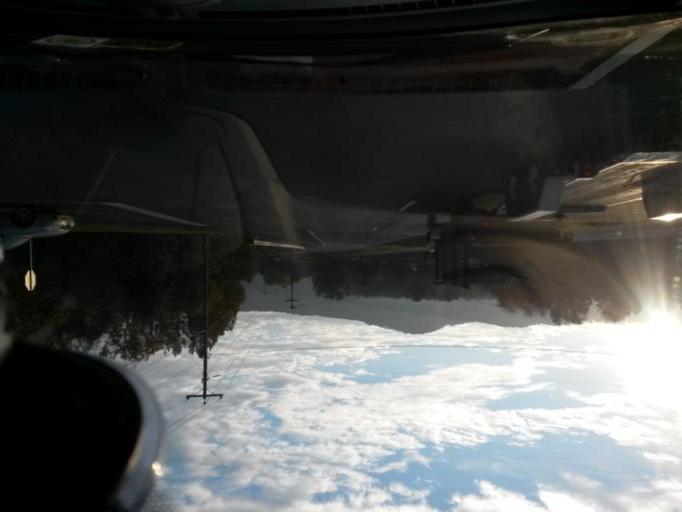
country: US
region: Virginia
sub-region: Botetourt County
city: Laymantown
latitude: 37.3331
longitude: -79.8740
